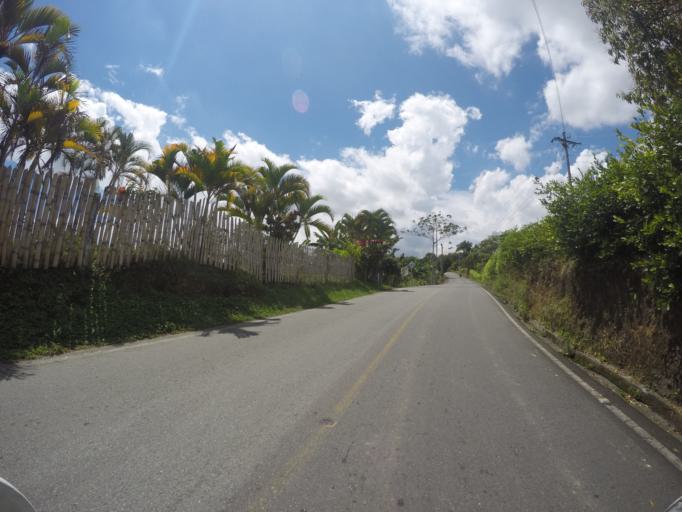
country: CO
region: Quindio
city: Quimbaya
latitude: 4.6275
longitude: -75.7380
